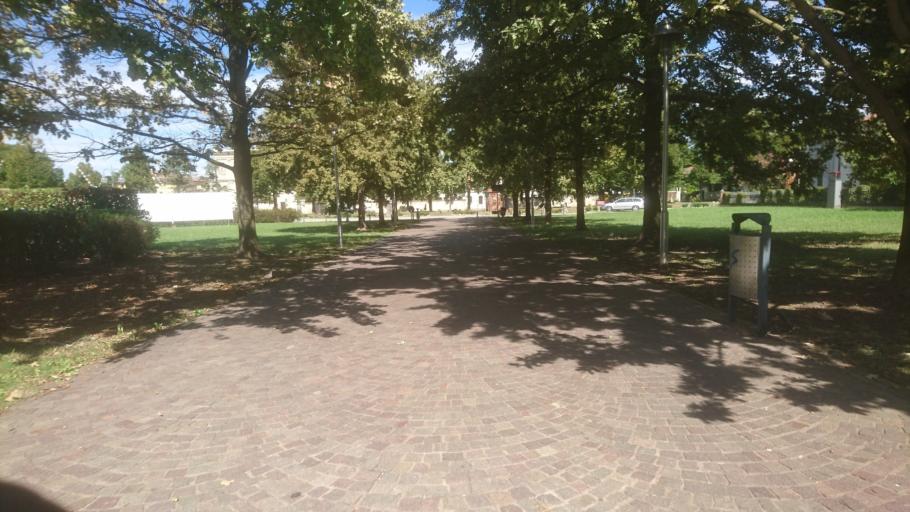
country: IT
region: Veneto
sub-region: Provincia di Venezia
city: Mira Taglio
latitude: 45.4334
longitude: 12.1329
